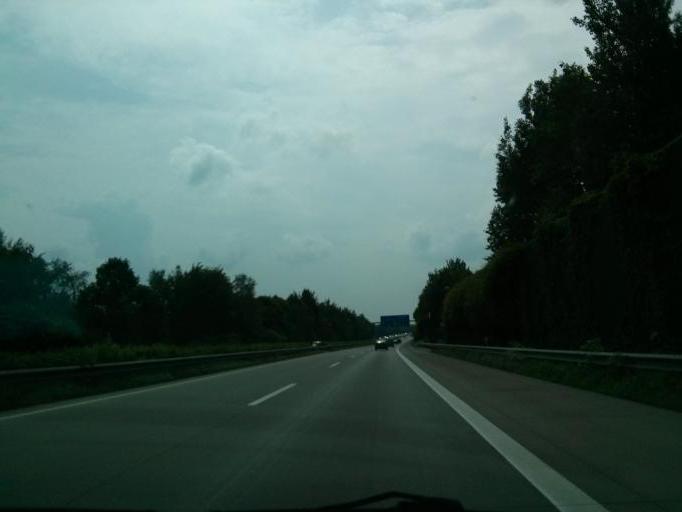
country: DE
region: Lower Saxony
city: Schiffdorf
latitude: 53.5069
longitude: 8.6290
